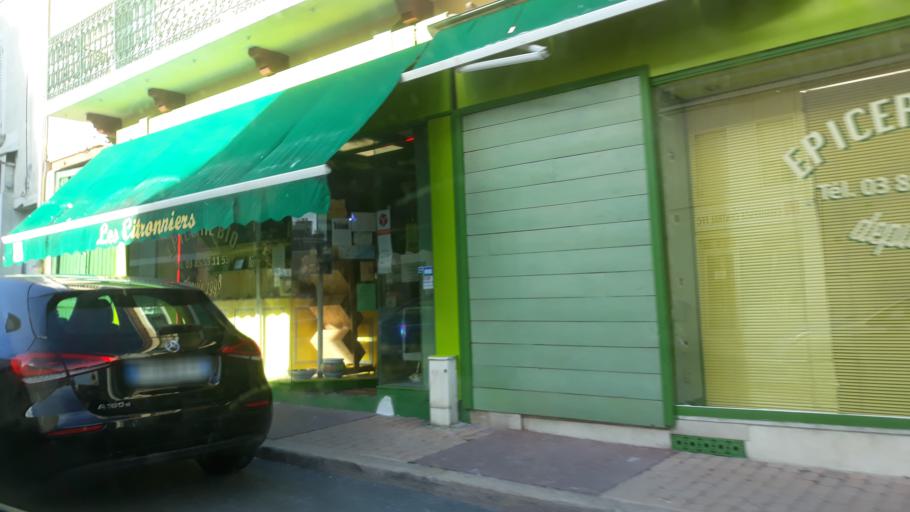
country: FR
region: Bourgogne
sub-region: Departement de Saone-et-Loire
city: Le Creusot
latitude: 46.7961
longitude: 4.4246
